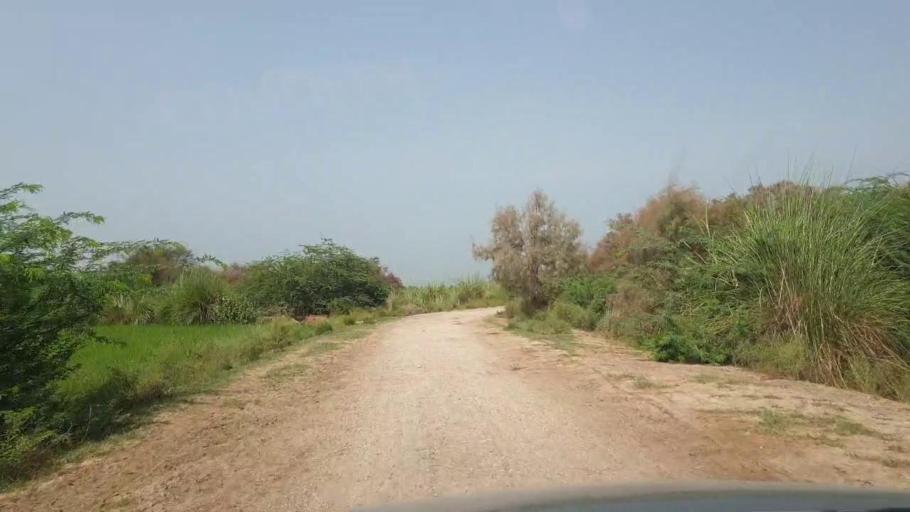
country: PK
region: Sindh
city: Madeji
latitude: 27.7958
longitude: 68.5400
